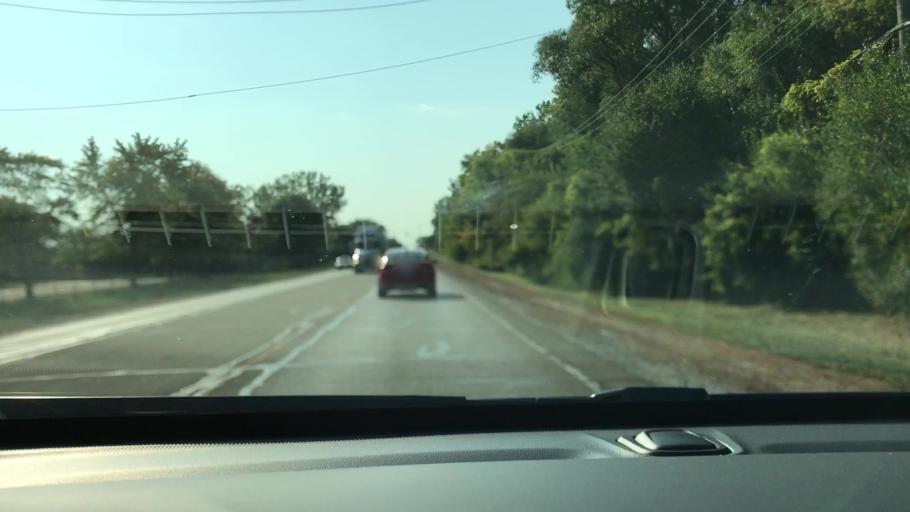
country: US
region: Illinois
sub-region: DuPage County
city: Warrenville
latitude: 41.7815
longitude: -88.2174
